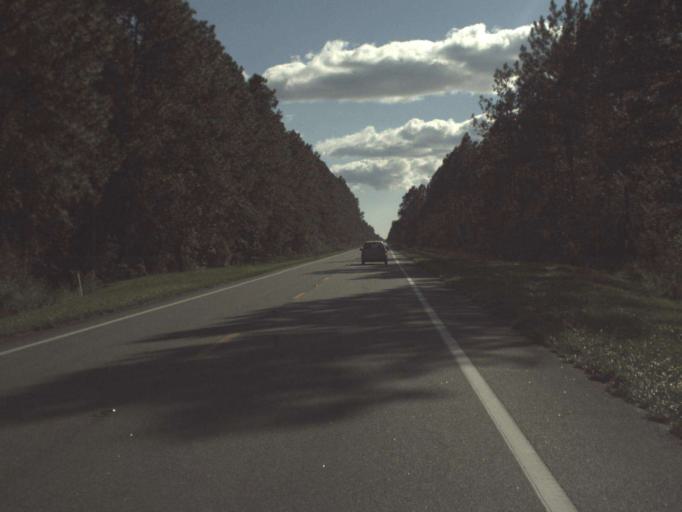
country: US
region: Florida
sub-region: Gulf County
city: Port Saint Joe
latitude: 29.9321
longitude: -85.1925
